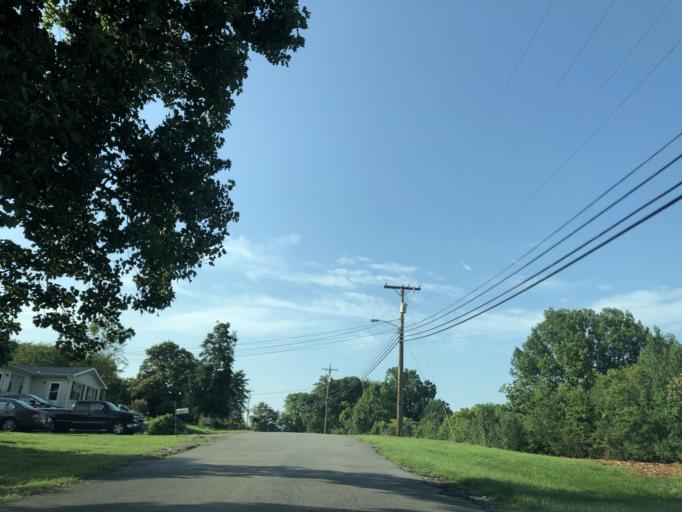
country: US
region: Tennessee
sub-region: Davidson County
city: Lakewood
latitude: 36.1479
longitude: -86.6585
